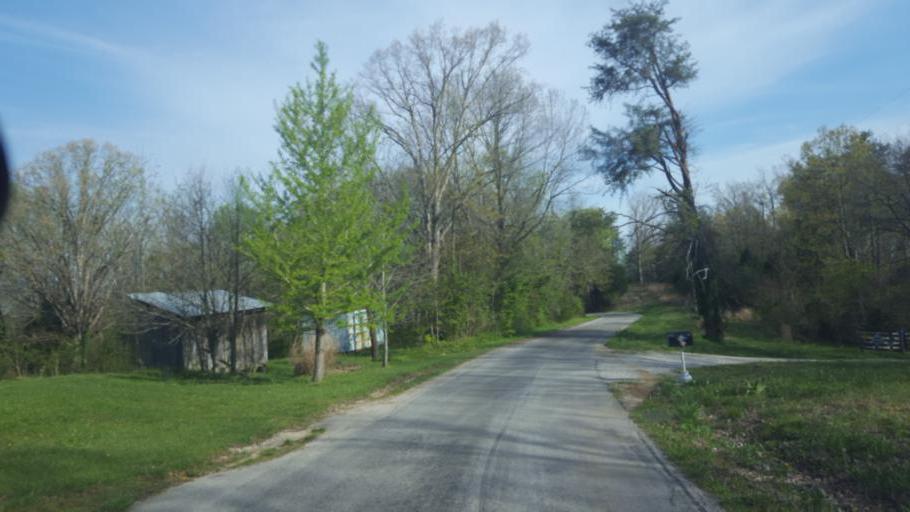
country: US
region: Kentucky
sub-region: Hart County
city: Munfordville
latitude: 37.3251
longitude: -86.0959
